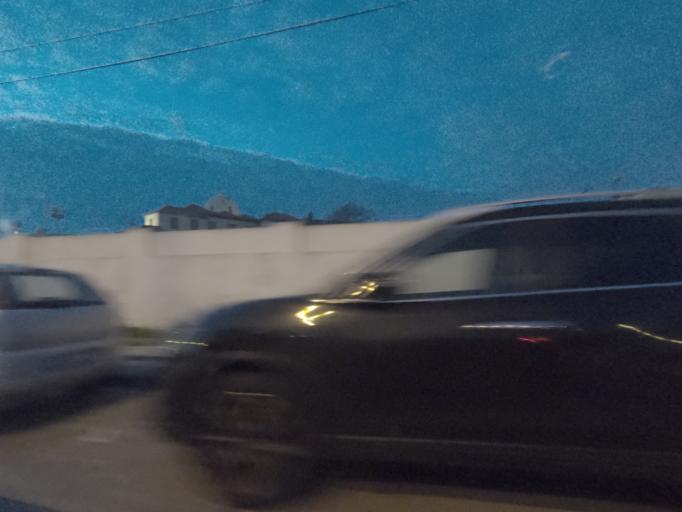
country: PT
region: Porto
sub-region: Vila Nova de Gaia
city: Canidelo
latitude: 41.1489
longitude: -8.6731
